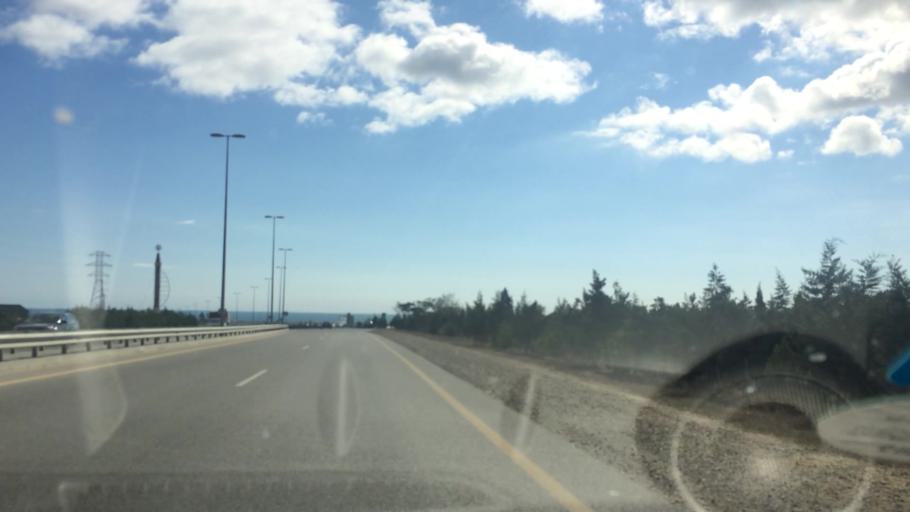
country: AZ
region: Baki
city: Zyrya
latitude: 40.4019
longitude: 50.3089
